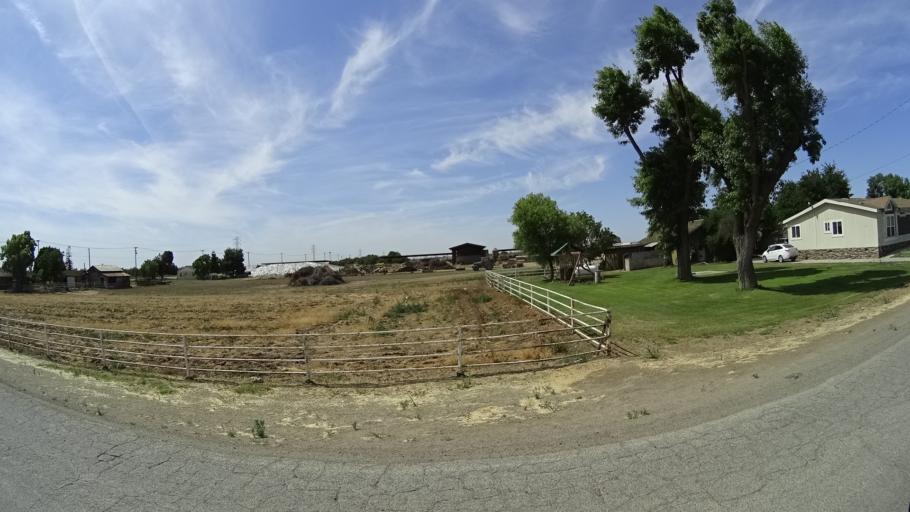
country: US
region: California
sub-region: Kings County
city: Hanford
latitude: 36.3572
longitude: -119.5935
